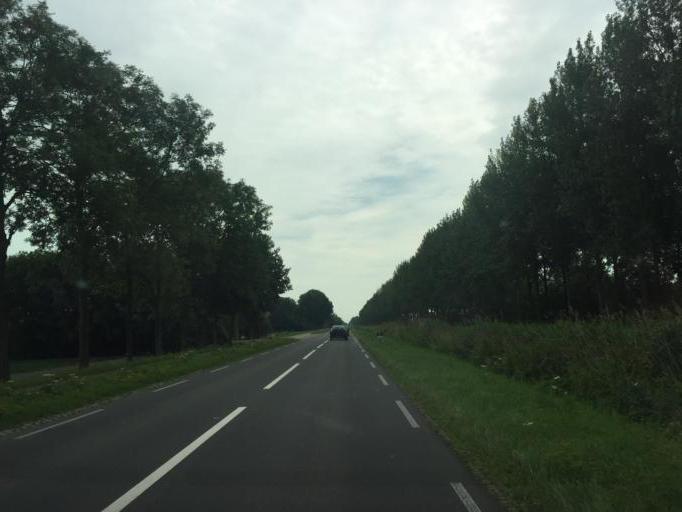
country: NL
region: North Holland
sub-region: Gemeente Alkmaar
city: Alkmaar
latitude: 52.6149
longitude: 4.8053
